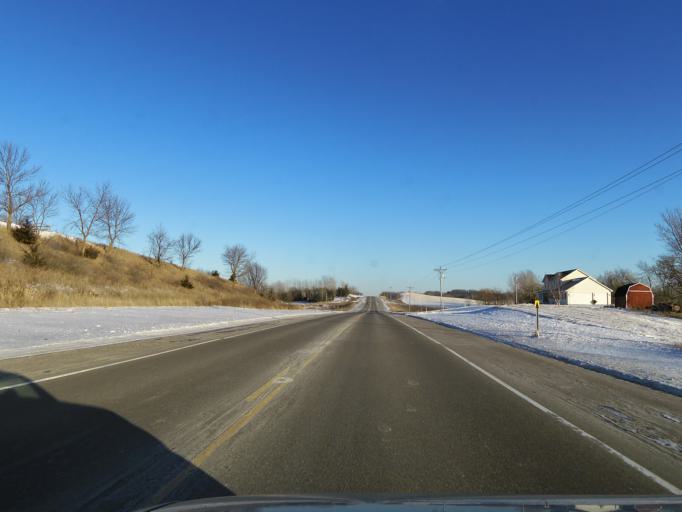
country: US
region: Minnesota
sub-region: Rice County
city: Lonsdale
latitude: 44.5438
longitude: -93.4051
